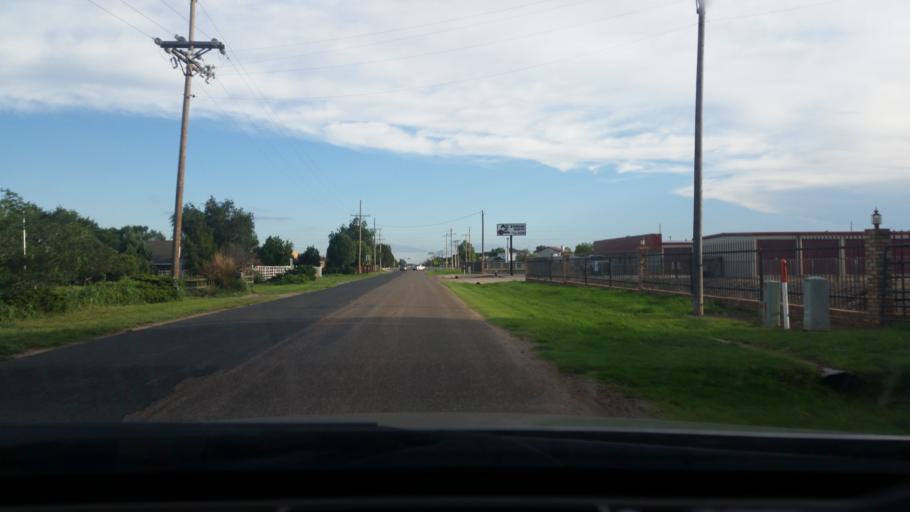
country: US
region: New Mexico
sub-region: Curry County
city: Clovis
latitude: 34.4505
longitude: -103.1785
